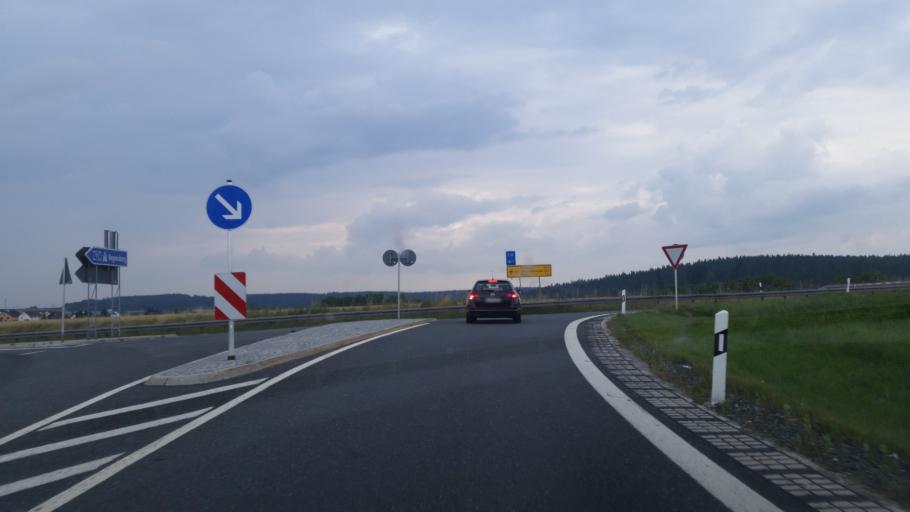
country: DE
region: Bavaria
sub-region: Upper Franconia
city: Rehau
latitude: 50.2463
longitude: 12.0586
